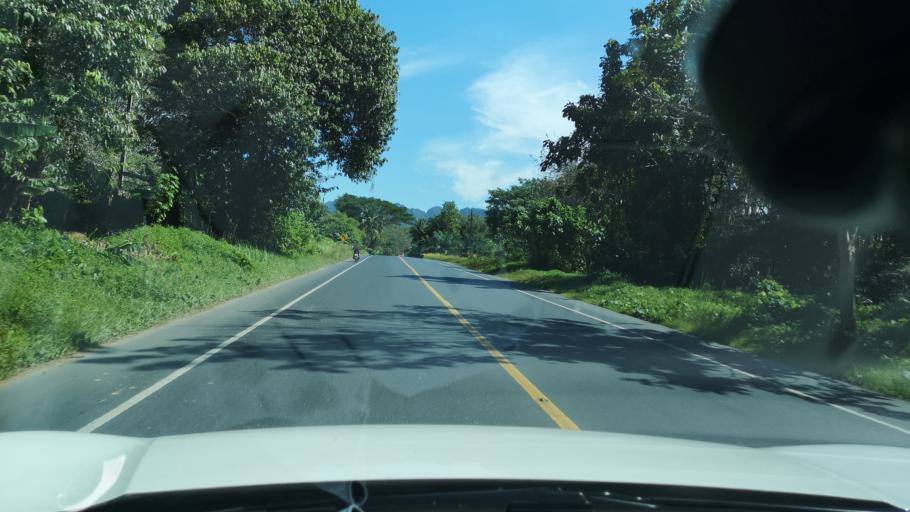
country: TH
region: Phangnga
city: Phang Nga
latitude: 8.5359
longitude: 98.5004
